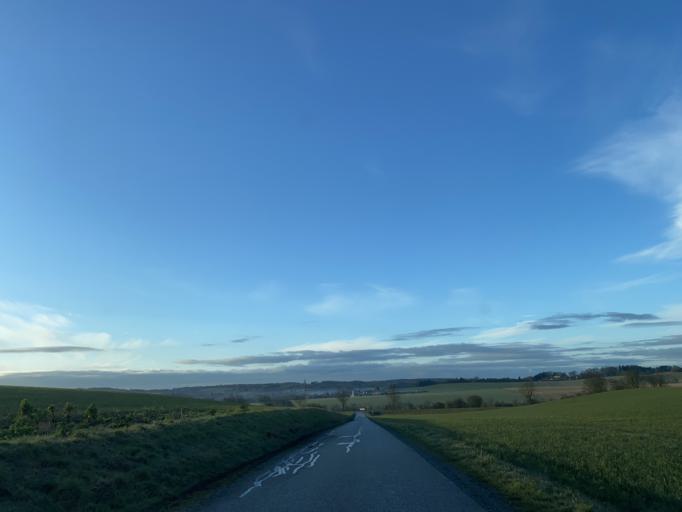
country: DK
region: Central Jutland
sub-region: Favrskov Kommune
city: Hammel
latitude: 56.2412
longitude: 9.7388
